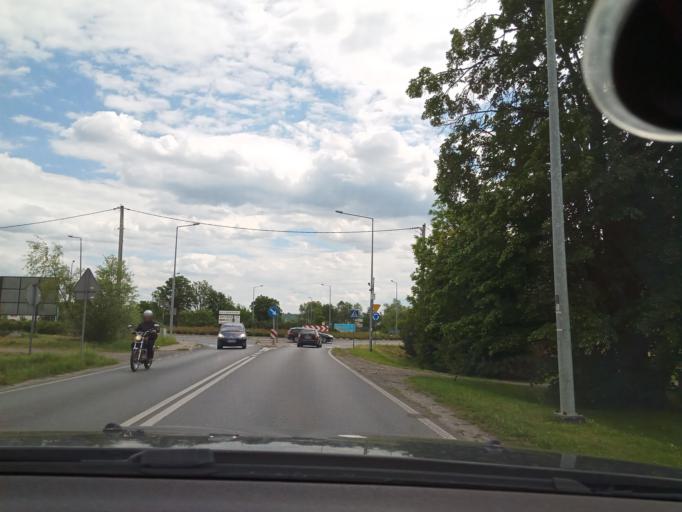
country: PL
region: Lesser Poland Voivodeship
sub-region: Powiat wielicki
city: Gdow
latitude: 49.9152
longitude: 20.1933
